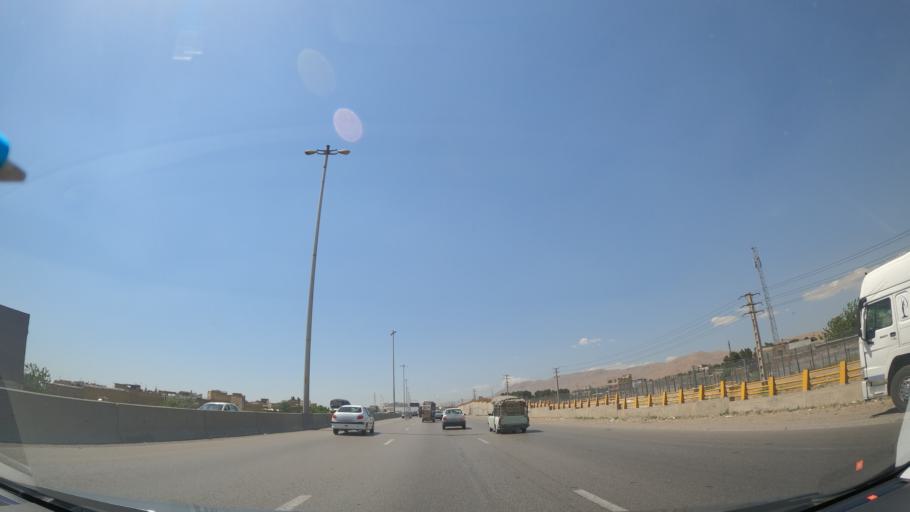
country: IR
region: Alborz
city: Karaj
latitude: 35.8651
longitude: 50.9031
